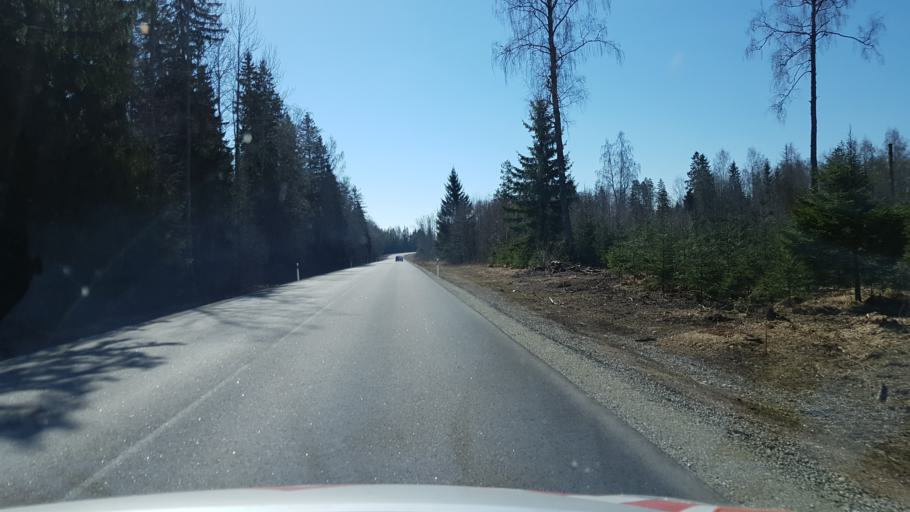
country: EE
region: Laeaene-Virumaa
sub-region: Vinni vald
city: Vinni
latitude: 59.1235
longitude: 26.6168
